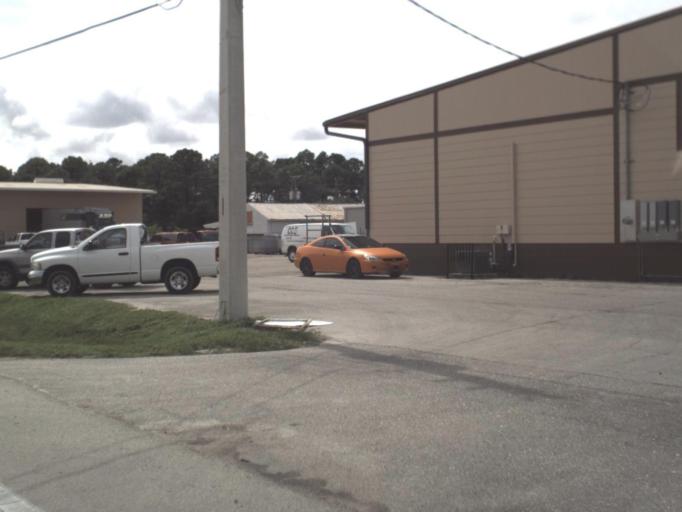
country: US
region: Florida
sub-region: Lee County
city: Fort Myers
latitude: 26.6132
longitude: -81.8518
